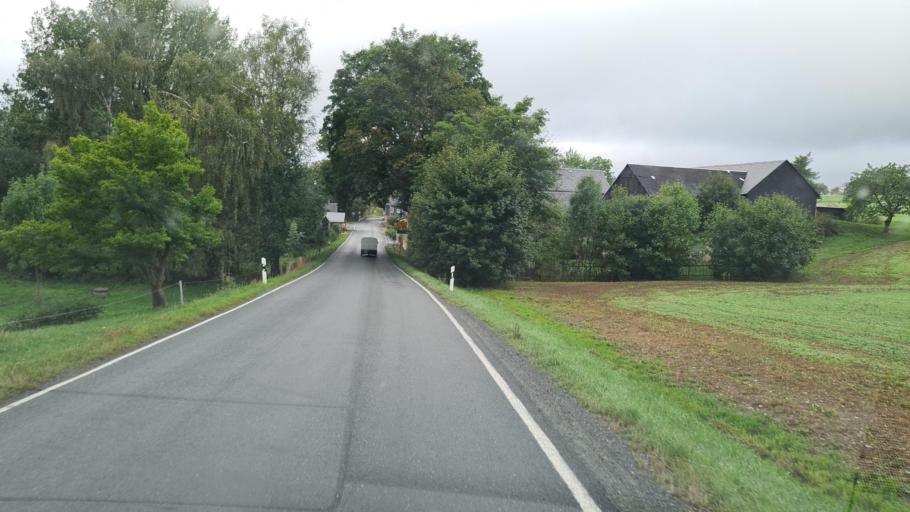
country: DE
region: Thuringia
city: Wurzbach
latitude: 50.5286
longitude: 11.5312
